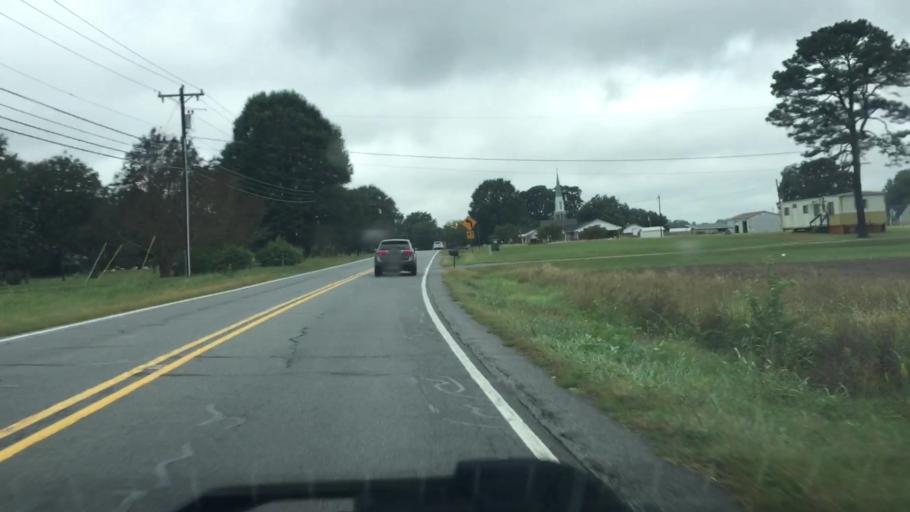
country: US
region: North Carolina
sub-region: Rowan County
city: China Grove
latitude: 35.6526
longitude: -80.5781
